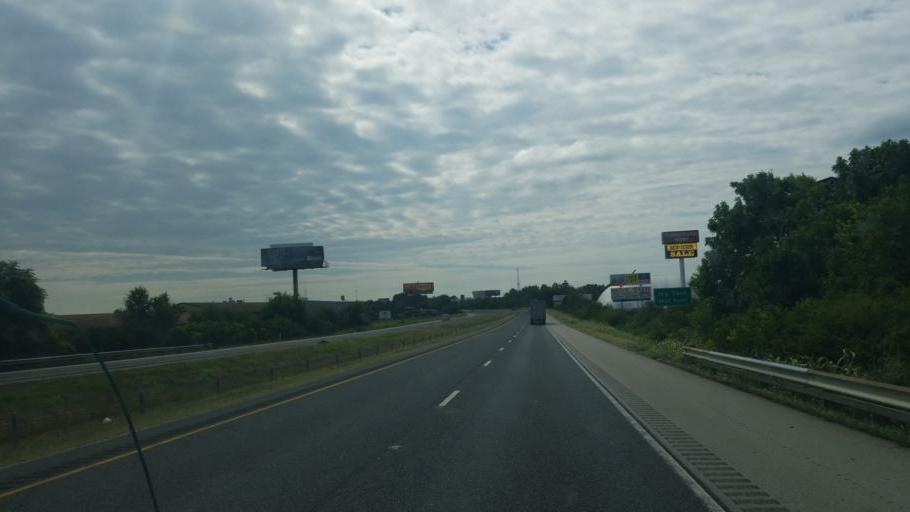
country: US
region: Indiana
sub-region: Vigo County
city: Terre Haute
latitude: 39.4334
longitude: -87.4253
